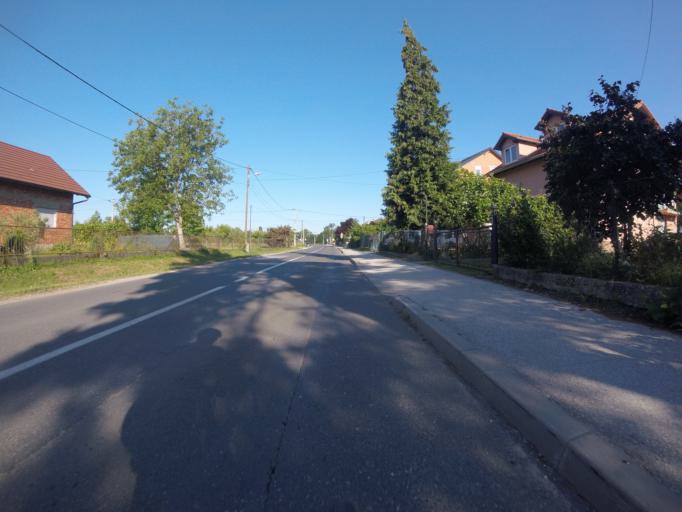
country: HR
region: Grad Zagreb
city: Zadvorsko
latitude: 45.7266
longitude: 15.9142
